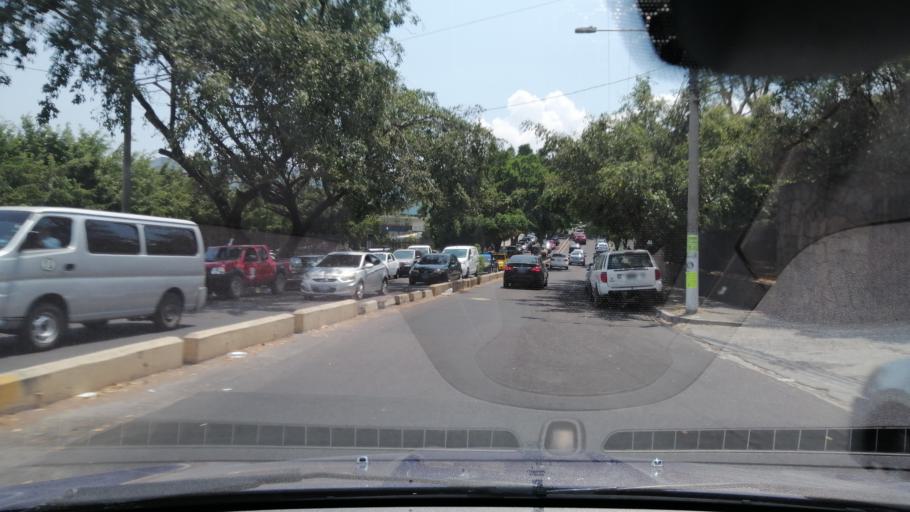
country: SV
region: San Salvador
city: San Salvador
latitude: 13.7051
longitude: -89.2021
